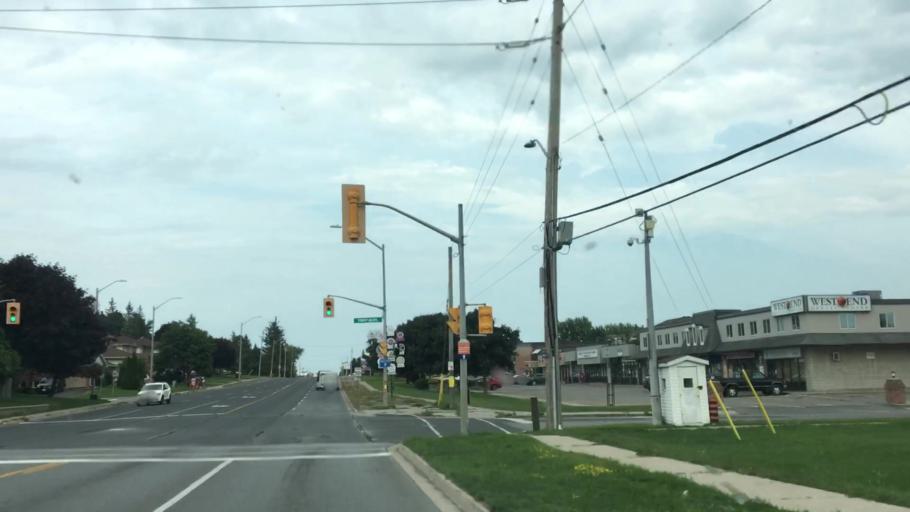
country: CA
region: Ontario
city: Quinte West
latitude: 44.0945
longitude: -77.5979
